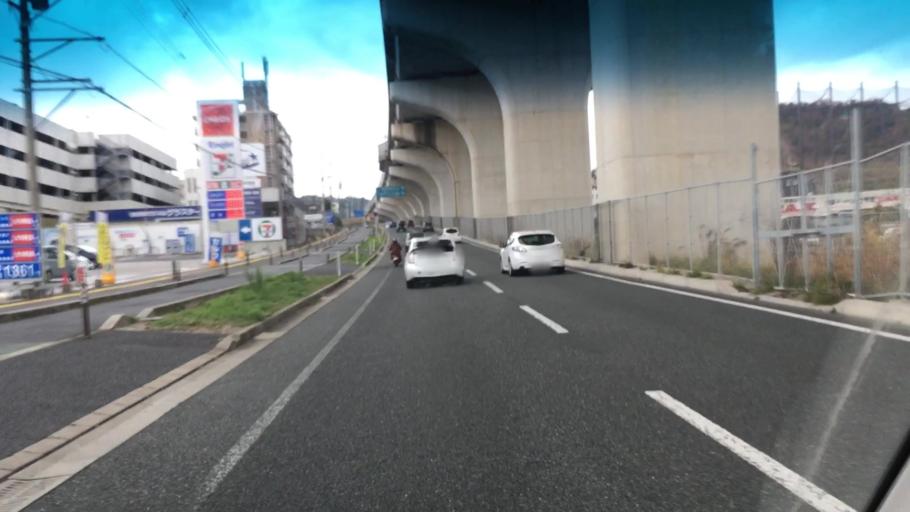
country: JP
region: Fukuoka
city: Maebaru-chuo
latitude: 33.5692
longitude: 130.3006
